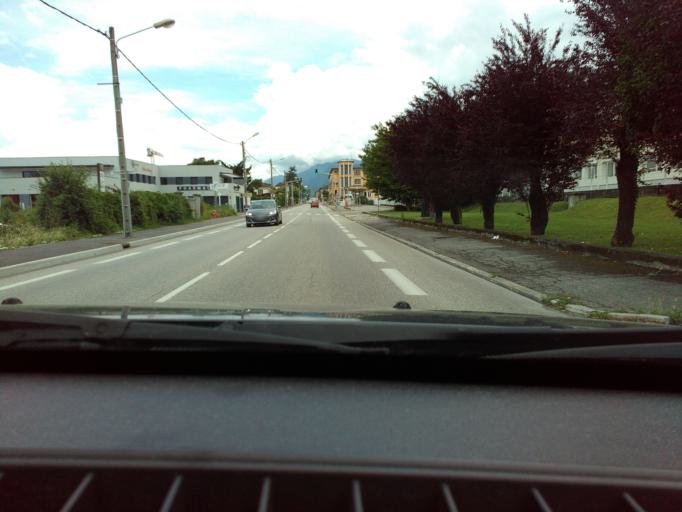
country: FR
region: Rhone-Alpes
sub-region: Departement de l'Isere
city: Froges
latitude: 45.2698
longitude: 5.9207
